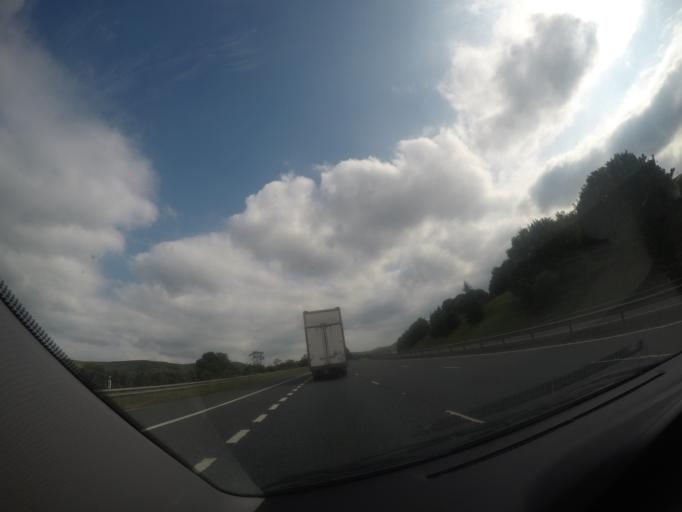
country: GB
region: Scotland
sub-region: South Lanarkshire
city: Douglas
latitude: 55.4999
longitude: -3.6941
